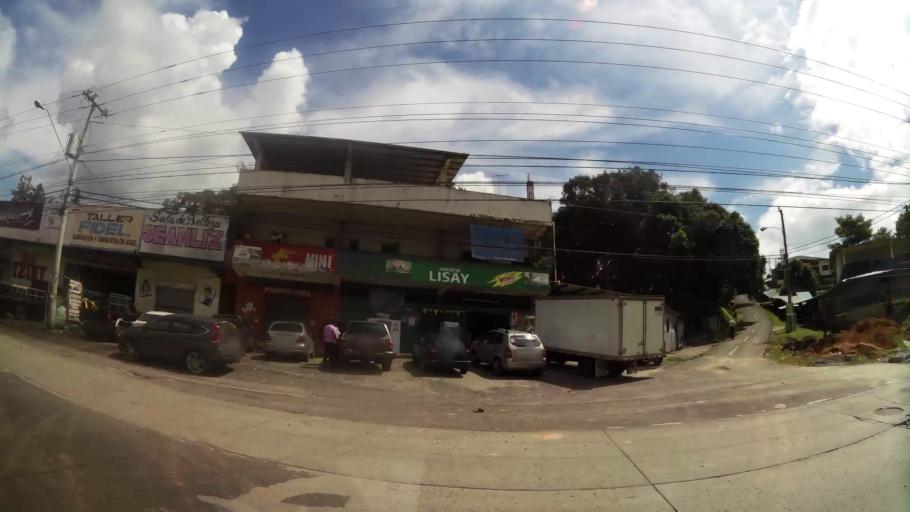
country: PA
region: Panama
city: Vista Alegre
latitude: 8.9414
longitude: -79.6792
